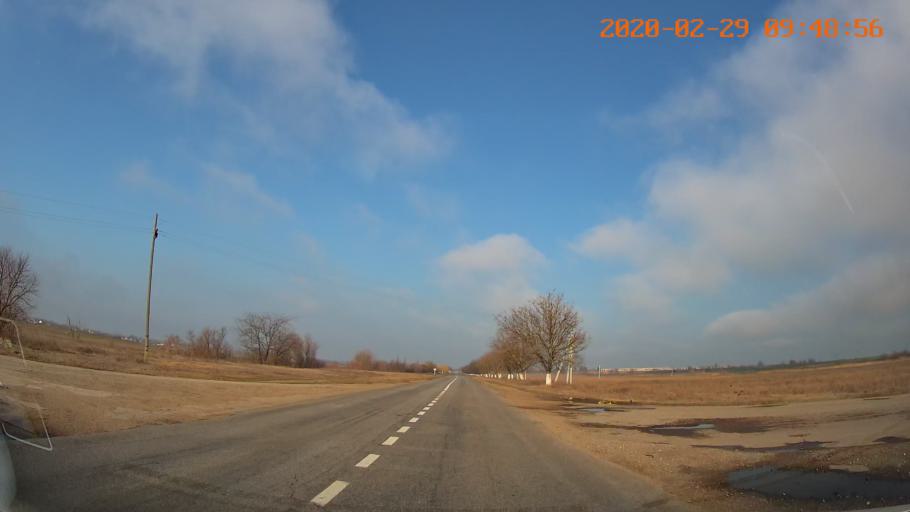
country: MD
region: Telenesti
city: Crasnoe
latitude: 46.6935
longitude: 29.7800
